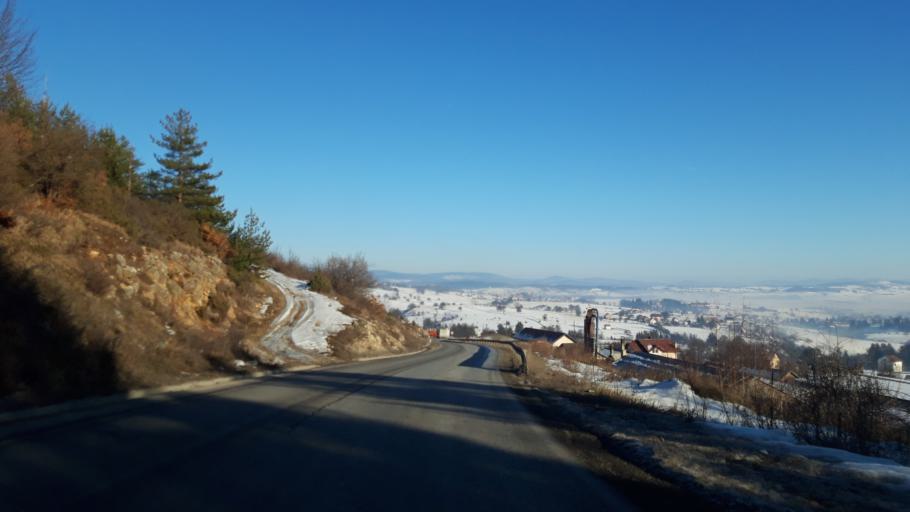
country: BA
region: Republika Srpska
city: Sokolac
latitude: 43.9225
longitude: 18.7490
